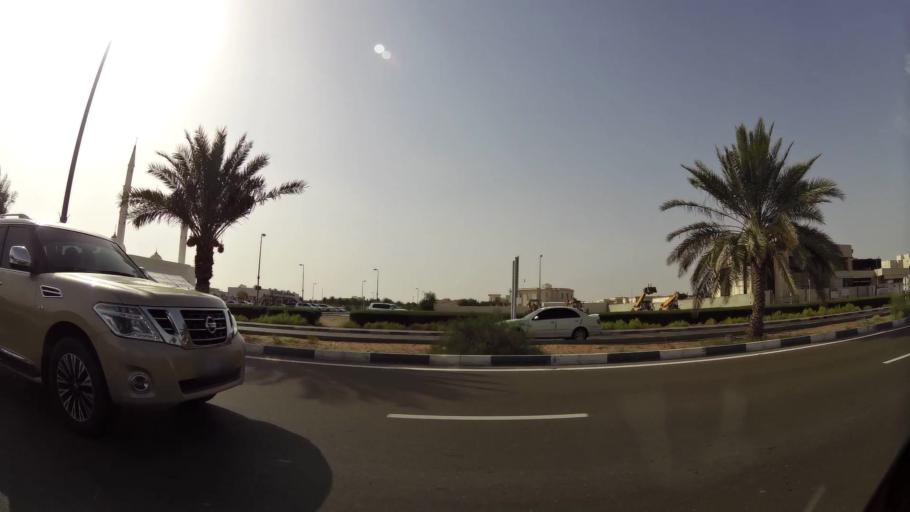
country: AE
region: Abu Dhabi
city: Al Ain
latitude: 24.2272
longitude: 55.6631
